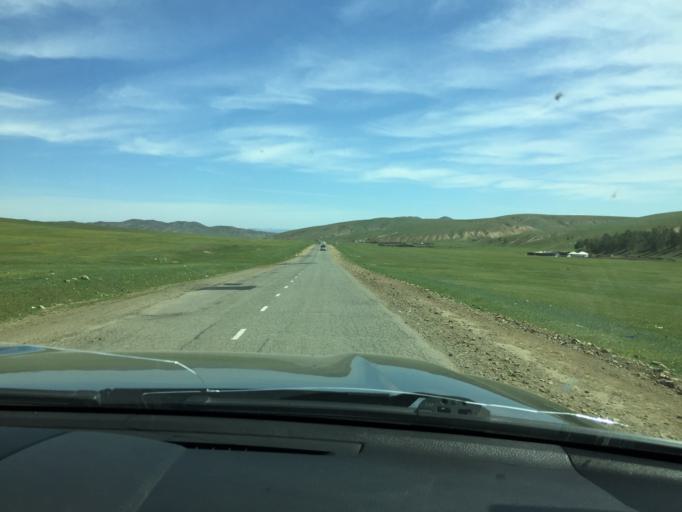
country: MN
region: Central Aimak
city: Javhlant
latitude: 48.6598
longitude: 106.1202
